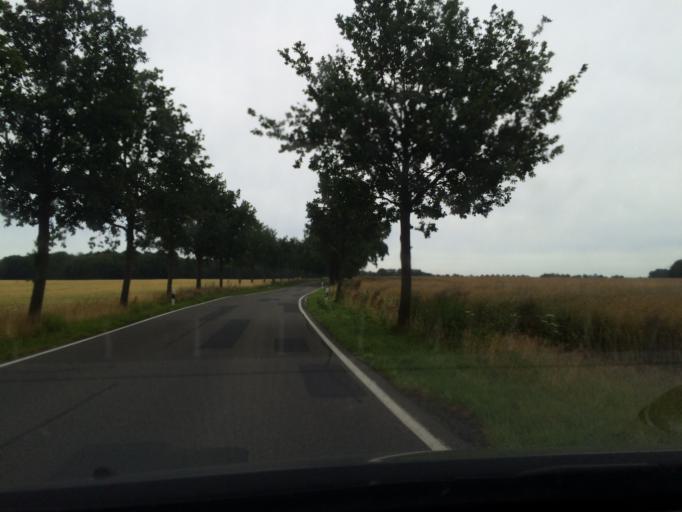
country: DE
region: Mecklenburg-Vorpommern
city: Prohn
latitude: 54.3883
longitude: 13.0031
